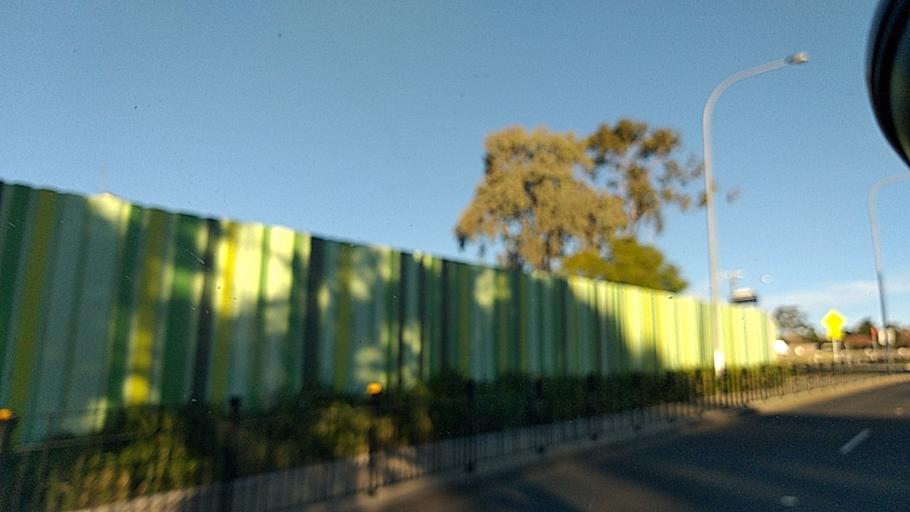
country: AU
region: New South Wales
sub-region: Campbelltown Municipality
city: Campbelltown
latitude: -34.0612
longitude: 150.8252
